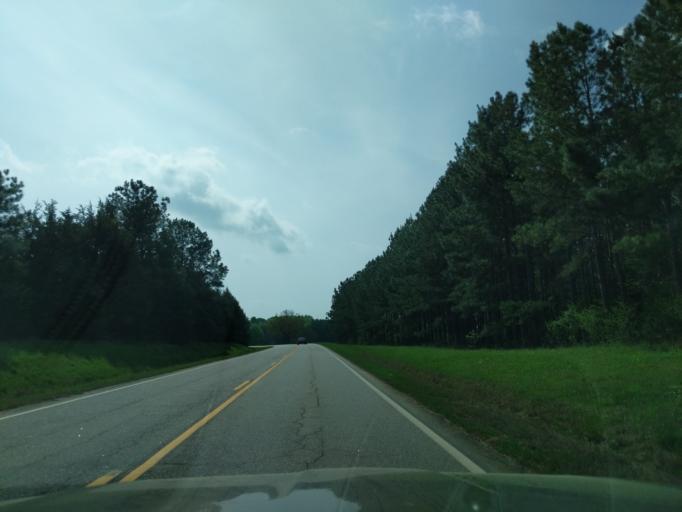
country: US
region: Georgia
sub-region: Lincoln County
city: Lincolnton
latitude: 33.7950
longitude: -82.3853
